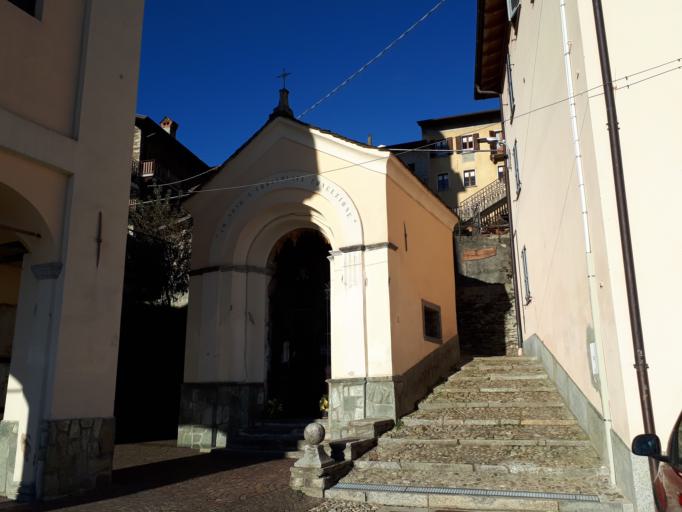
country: IT
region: Lombardy
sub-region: Provincia di Como
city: Dosso del Liro
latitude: 46.1637
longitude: 9.2743
